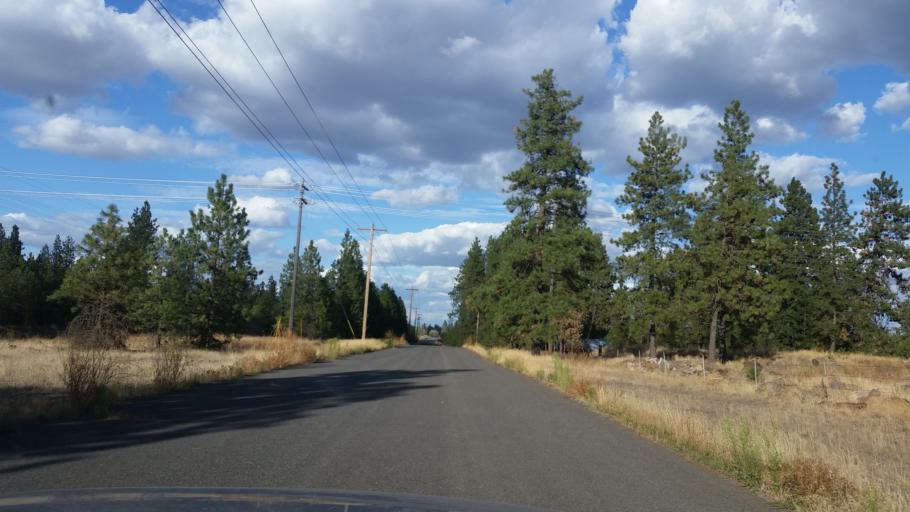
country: US
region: Washington
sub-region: Spokane County
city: Cheney
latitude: 47.4786
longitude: -117.5841
